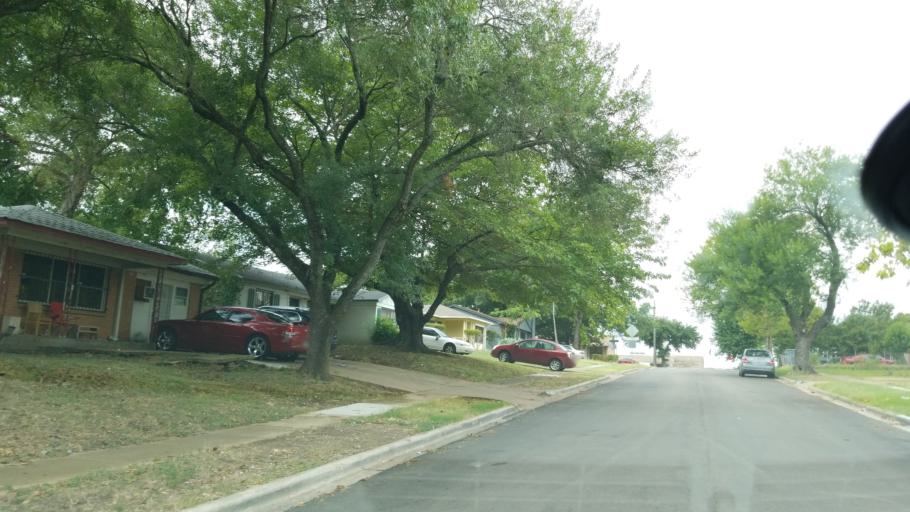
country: US
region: Texas
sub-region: Dallas County
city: Duncanville
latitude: 32.6607
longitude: -96.8384
